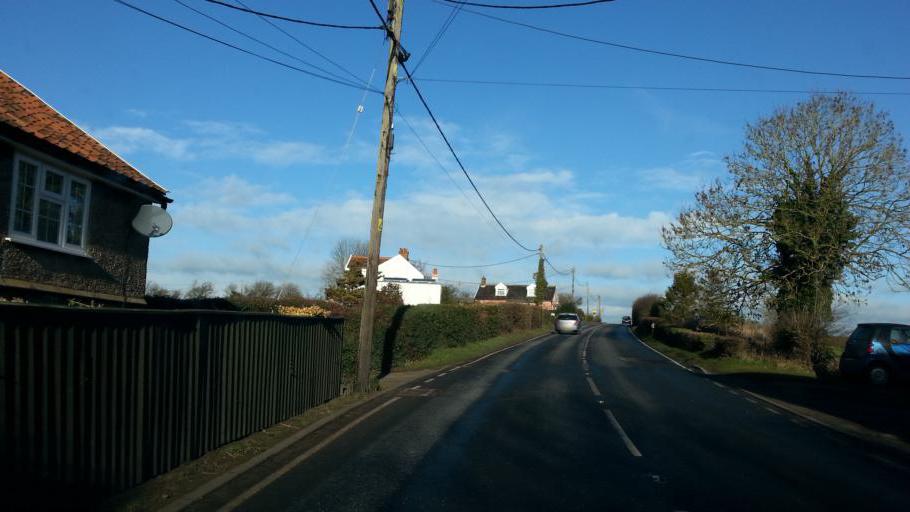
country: GB
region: England
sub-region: Suffolk
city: Halesworth
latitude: 52.3148
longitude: 1.5191
